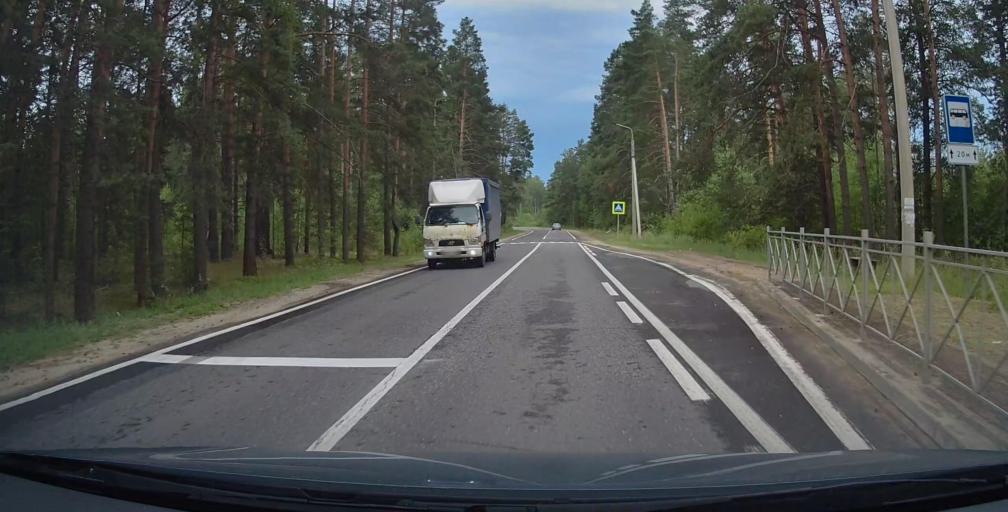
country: RU
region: Jaroslavl
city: Myshkin
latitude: 57.7969
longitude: 38.4996
